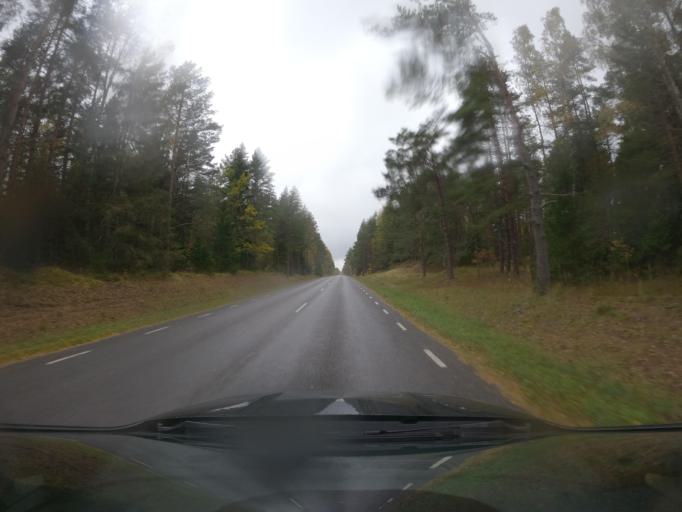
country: EE
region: Saare
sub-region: Kuressaare linn
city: Kuressaare
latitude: 58.3407
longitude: 22.1505
